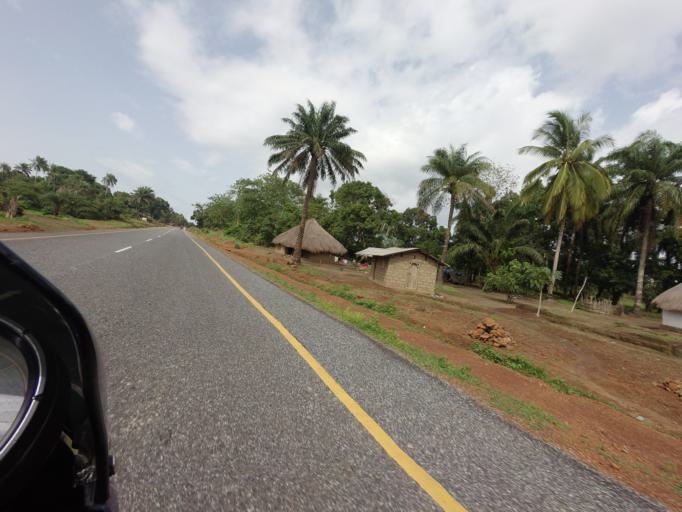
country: SL
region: Northern Province
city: Kambia
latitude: 9.0328
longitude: -12.9328
